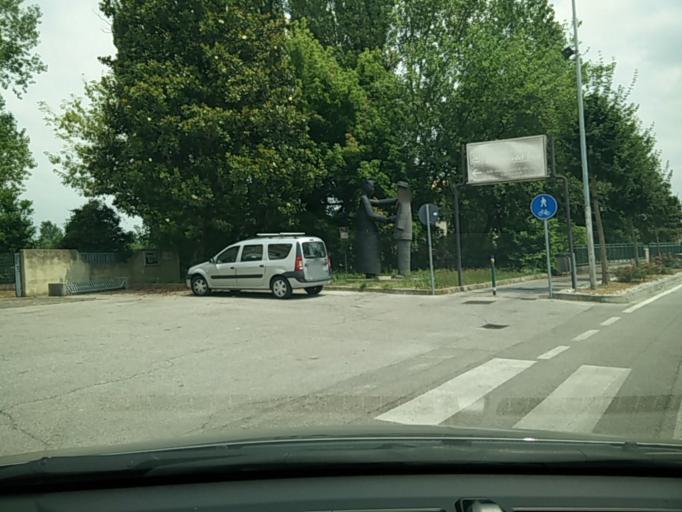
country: IT
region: Veneto
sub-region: Provincia di Venezia
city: Summaga
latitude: 45.7828
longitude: 12.7639
